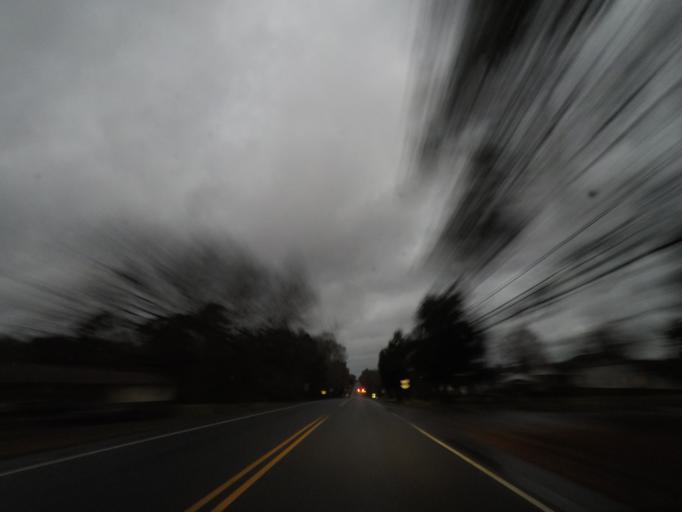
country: US
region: North Carolina
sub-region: Orange County
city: Hillsborough
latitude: 36.0896
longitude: -79.1035
